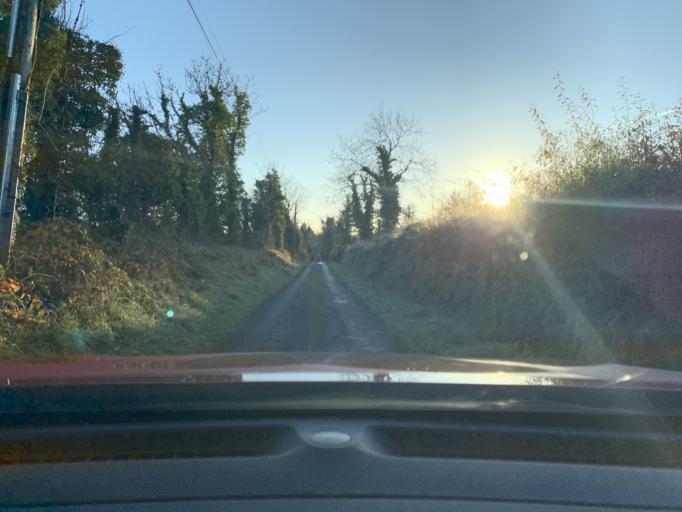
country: IE
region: Connaught
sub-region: Sligo
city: Ballymote
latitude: 53.9858
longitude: -8.5211
